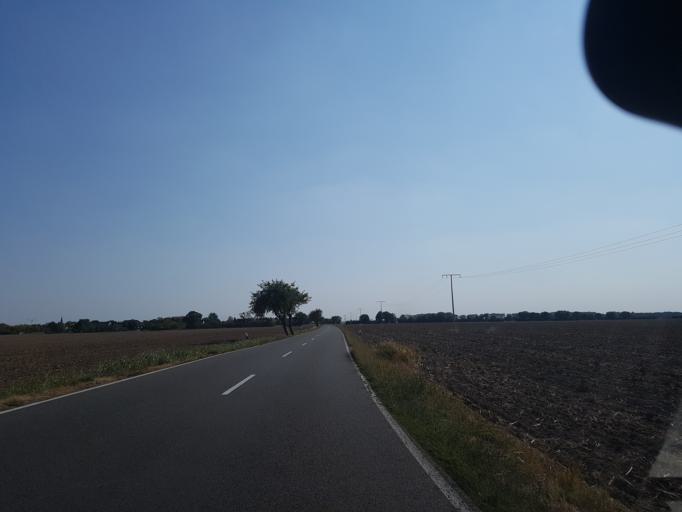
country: DE
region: Saxony-Anhalt
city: Annaburg
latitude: 51.6824
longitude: 12.9962
